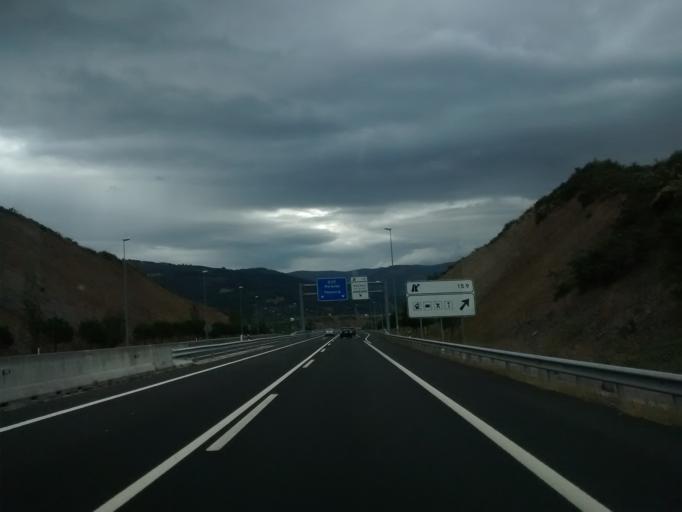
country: ES
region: Cantabria
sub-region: Provincia de Cantabria
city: Arenas de Iguna
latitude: 43.1884
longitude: -4.0652
